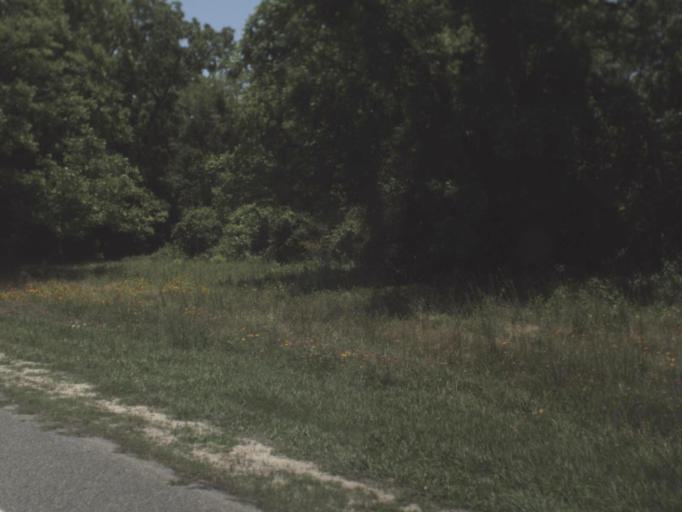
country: US
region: Florida
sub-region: Suwannee County
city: Live Oak
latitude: 30.3400
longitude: -83.0826
